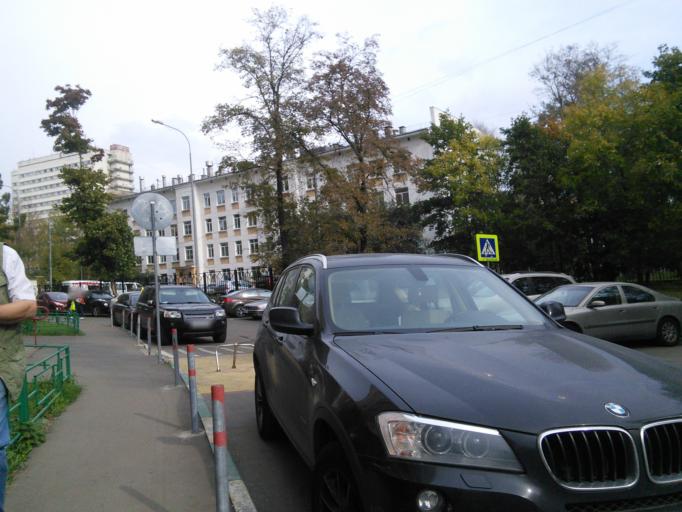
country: RU
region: Moskovskaya
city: Levoberezhnyy
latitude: 55.8657
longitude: 37.4744
